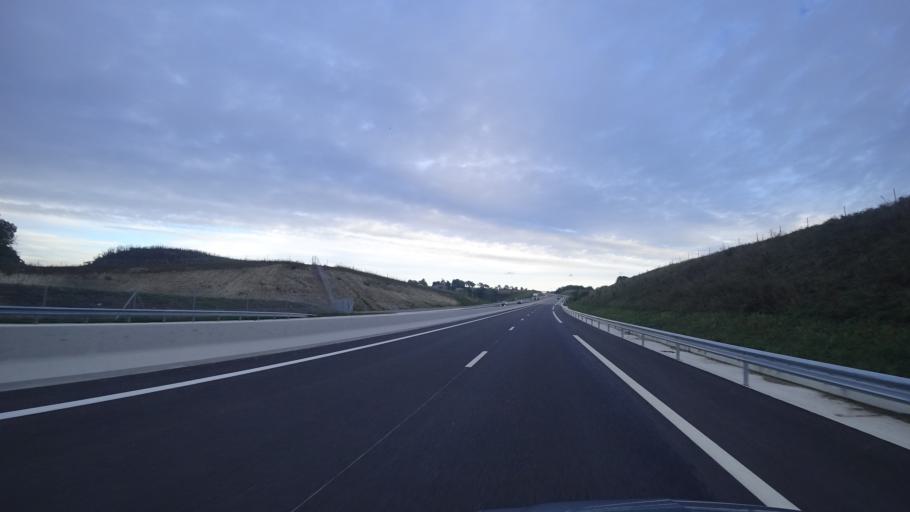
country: FR
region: Midi-Pyrenees
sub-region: Departement de l'Aveyron
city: Baraqueville
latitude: 44.2917
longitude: 2.4519
